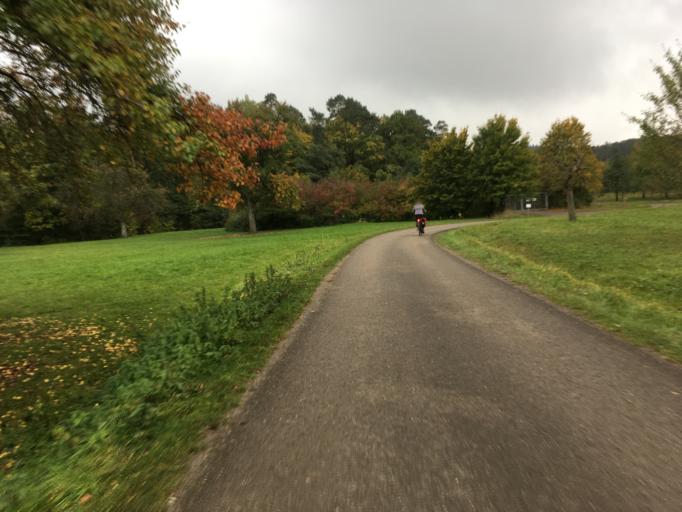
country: DE
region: Baden-Wuerttemberg
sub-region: Tuebingen Region
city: Nehren
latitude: 48.4244
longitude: 9.0806
